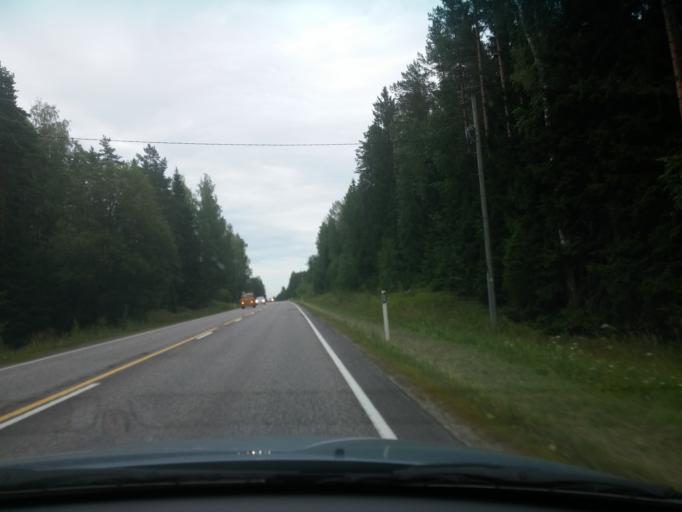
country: FI
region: Haeme
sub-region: Riihimaeki
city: Loppi
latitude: 60.7248
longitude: 24.4156
